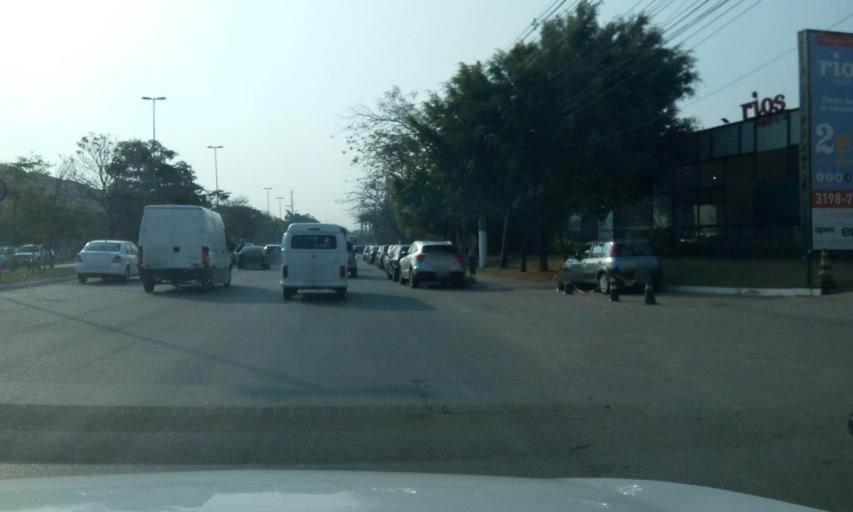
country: BR
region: Sao Paulo
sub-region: Diadema
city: Diadema
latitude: -23.6868
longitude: -46.6897
